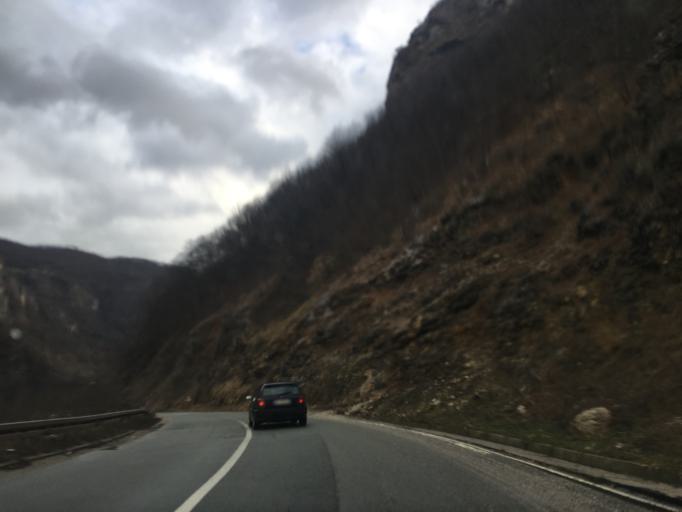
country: RS
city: Sokolovo Brdo
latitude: 43.1600
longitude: 19.7733
